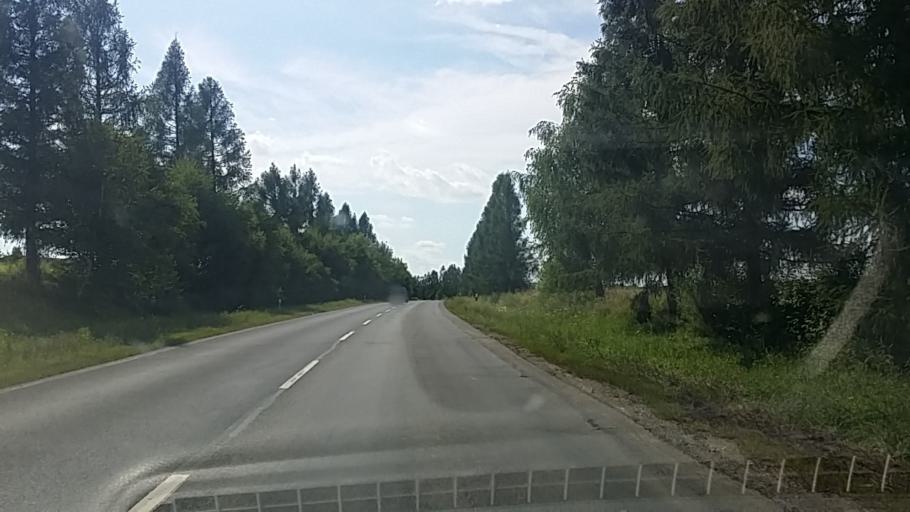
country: HU
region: Zala
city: Nagykanizsa
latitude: 46.4654
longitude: 17.0180
